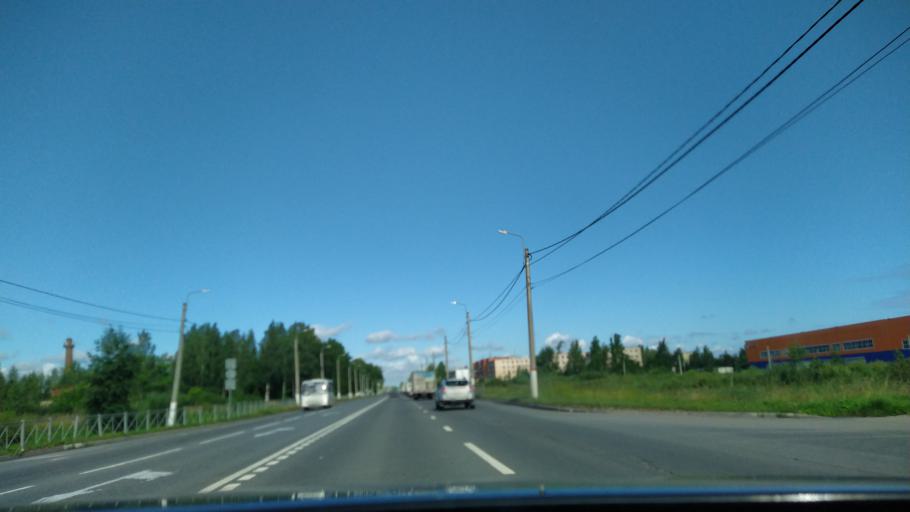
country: RU
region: Leningrad
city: Tosno
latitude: 59.5543
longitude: 30.8528
